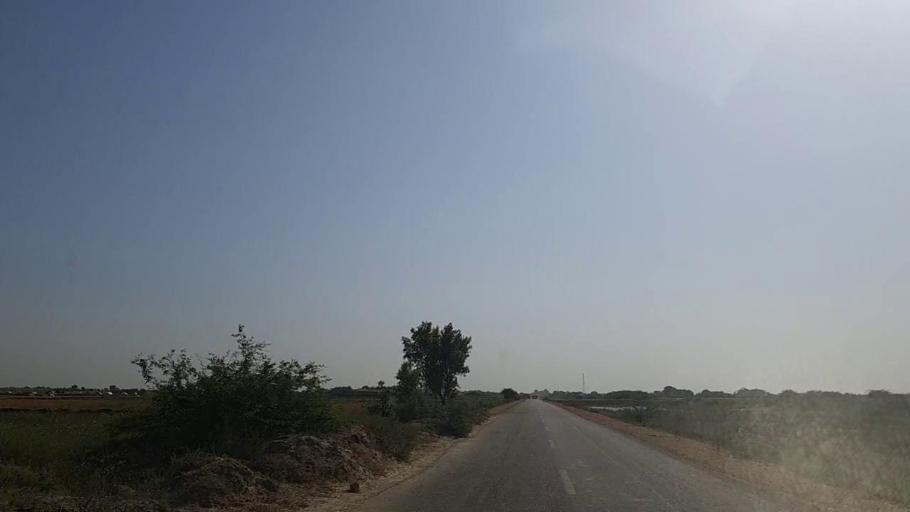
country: PK
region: Sindh
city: Jati
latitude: 24.5308
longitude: 68.2780
